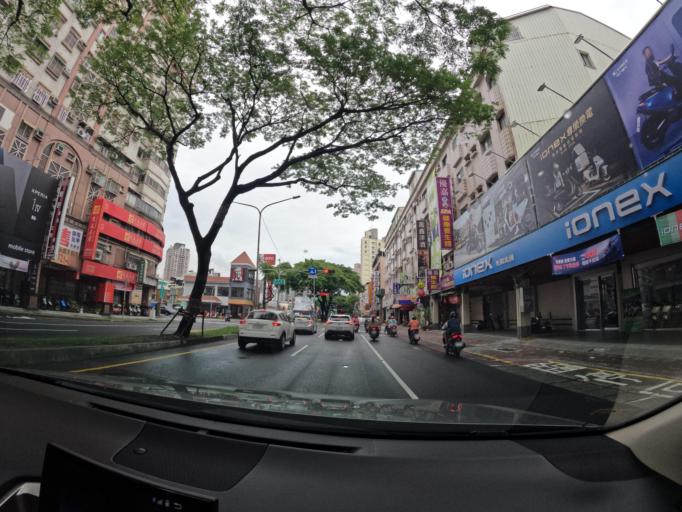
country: TW
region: Kaohsiung
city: Kaohsiung
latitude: 22.6450
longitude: 120.3259
